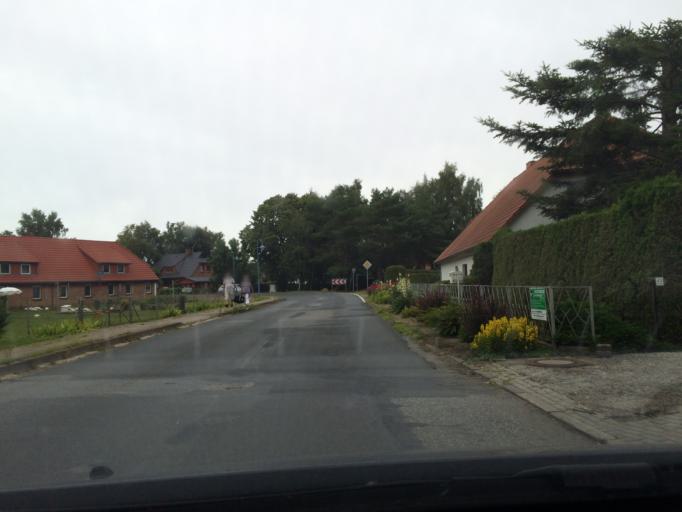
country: DE
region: Mecklenburg-Vorpommern
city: Prohn
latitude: 54.4115
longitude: 13.0156
